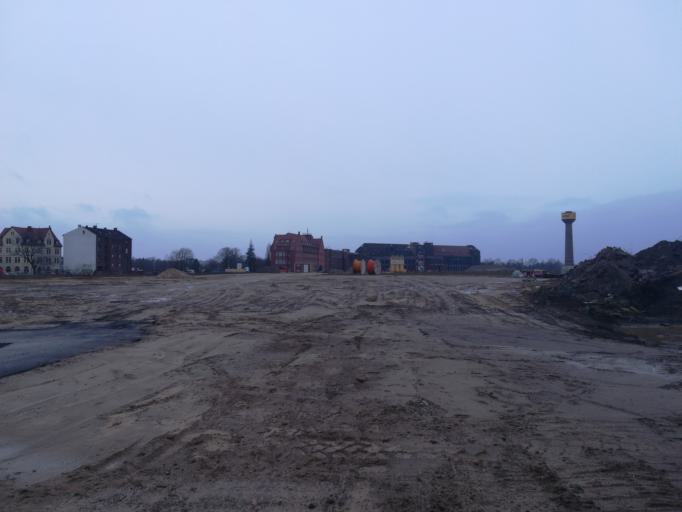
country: DE
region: Lower Saxony
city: Hannover
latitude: 52.3817
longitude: 9.6849
